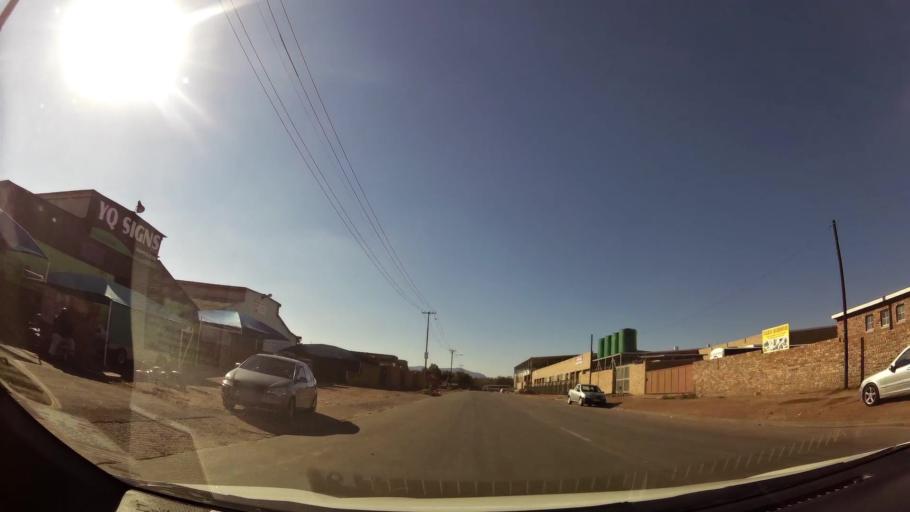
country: ZA
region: Limpopo
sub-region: Waterberg District Municipality
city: Mokopane
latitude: -24.1768
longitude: 29.0030
